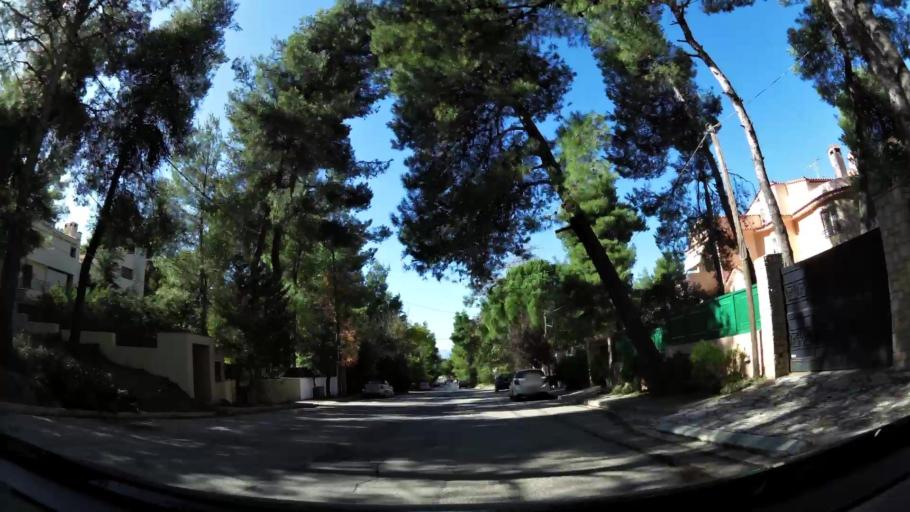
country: GR
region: Attica
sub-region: Nomarchia Anatolikis Attikis
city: Dionysos
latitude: 38.1065
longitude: 23.8865
